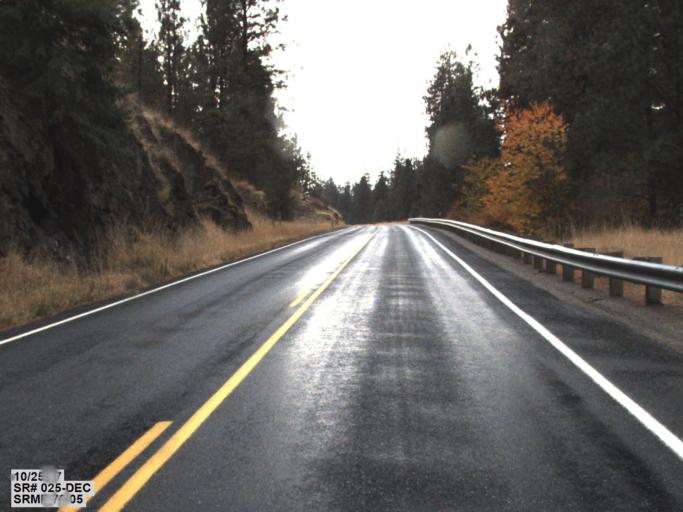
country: US
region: Washington
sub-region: Stevens County
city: Kettle Falls
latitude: 48.5020
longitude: -118.1564
